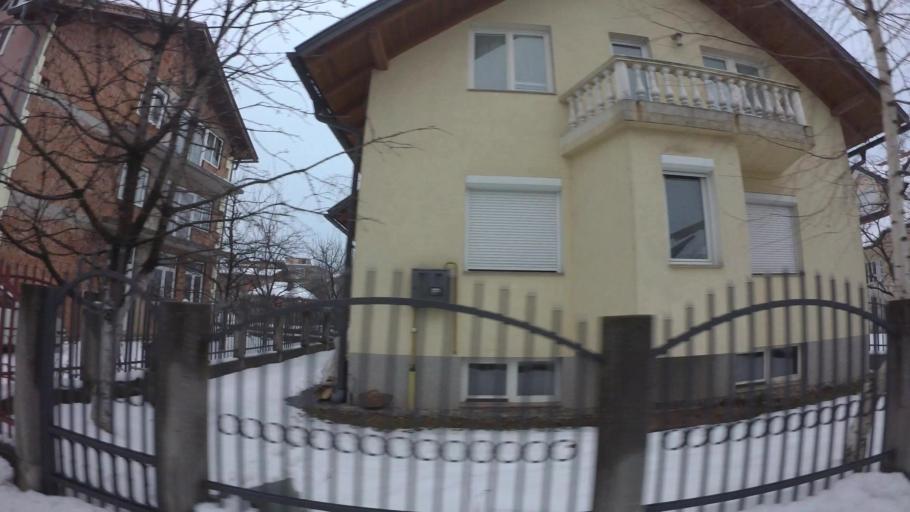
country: BA
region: Federation of Bosnia and Herzegovina
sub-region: Kanton Sarajevo
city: Sarajevo
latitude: 43.8431
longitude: 18.3132
